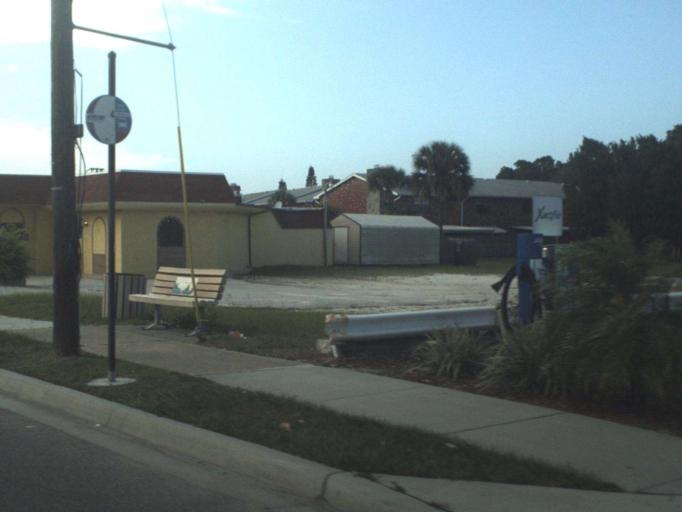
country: US
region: Florida
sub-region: Volusia County
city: South Daytona
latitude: 29.1681
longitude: -80.9999
